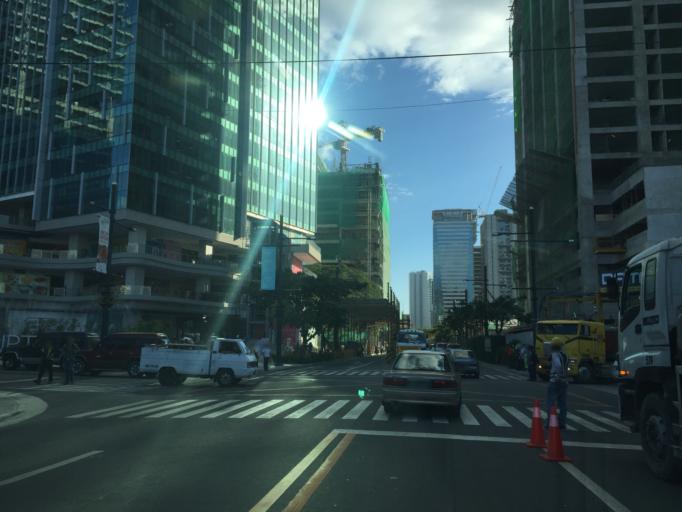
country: PH
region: Metro Manila
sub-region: Makati City
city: Makati City
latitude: 14.5575
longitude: 121.0536
